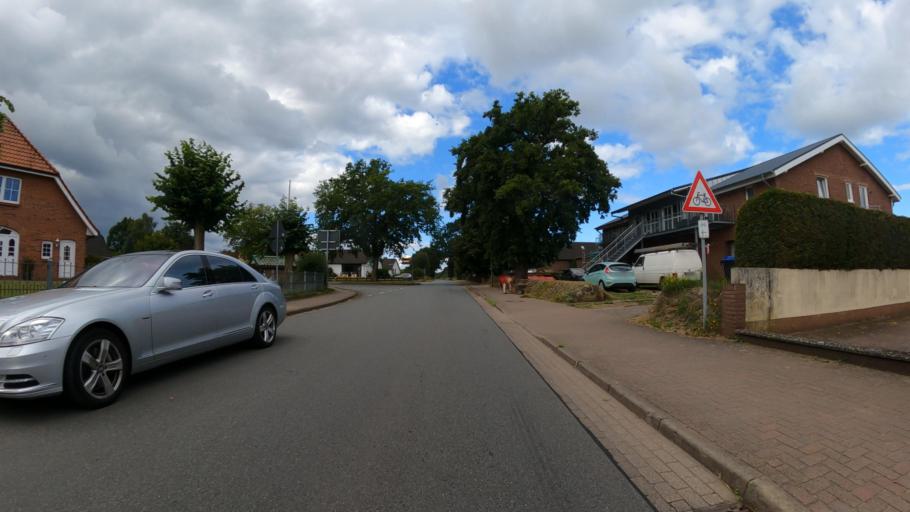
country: DE
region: Schleswig-Holstein
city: Padenstedt
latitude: 54.0489
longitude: 9.9164
